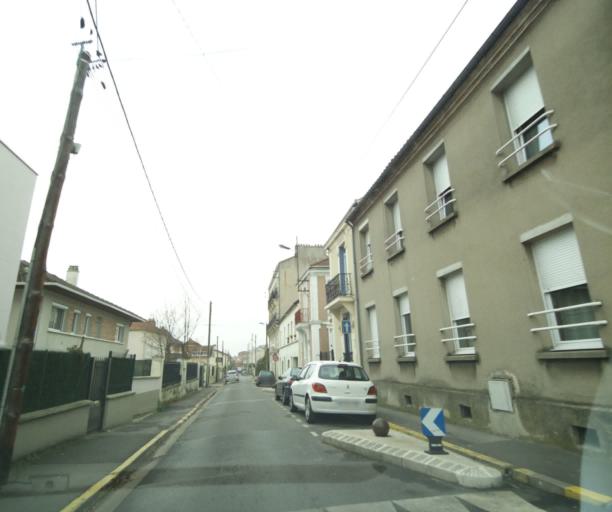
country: FR
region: Ile-de-France
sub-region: Departement de Seine-Saint-Denis
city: Livry-Gargan
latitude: 48.9234
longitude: 2.5420
